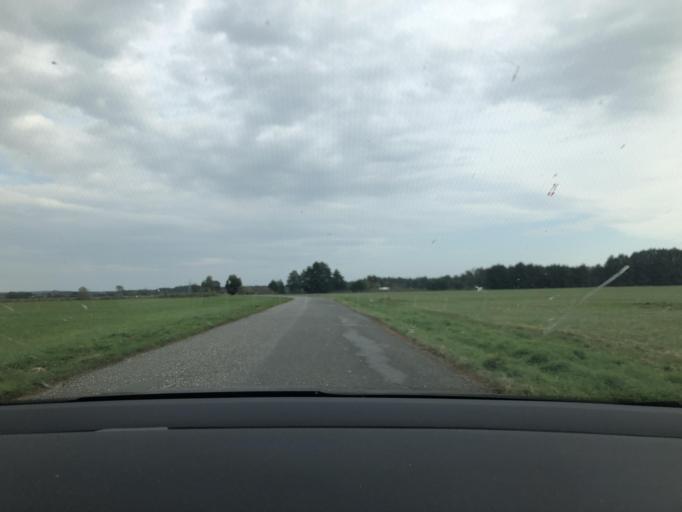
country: CZ
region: Pardubicky
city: Recany nad Labem
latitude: 50.0793
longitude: 15.4493
